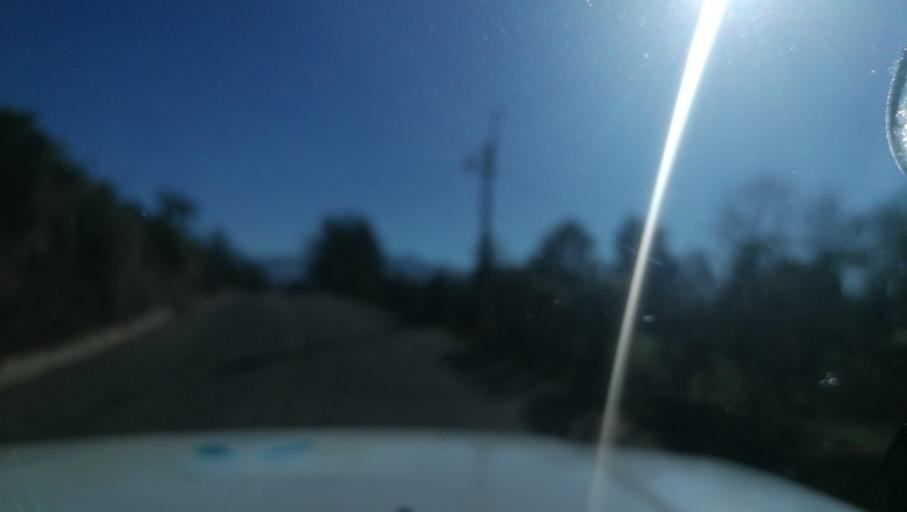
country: MX
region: Chiapas
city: Motozintla de Mendoza
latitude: 15.2376
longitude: -92.2339
